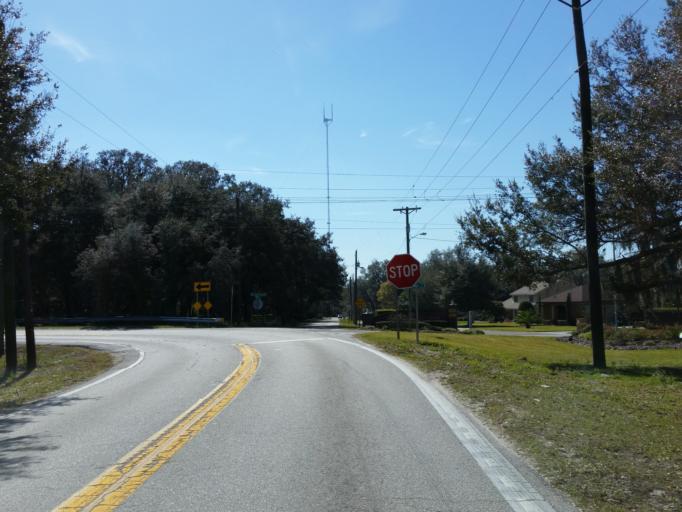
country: US
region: Florida
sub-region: Hillsborough County
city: Boyette
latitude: 27.8359
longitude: -82.2610
